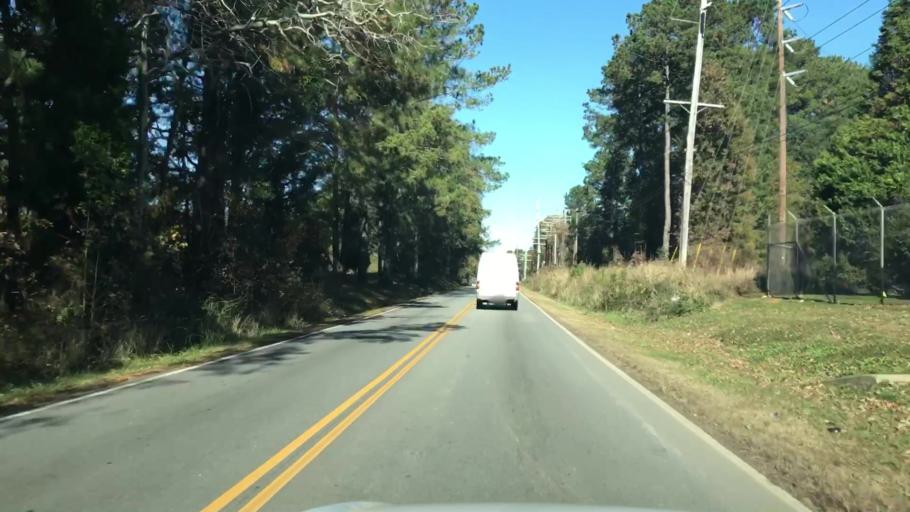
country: US
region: South Carolina
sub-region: Dorchester County
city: Centerville
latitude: 32.9859
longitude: -80.2204
